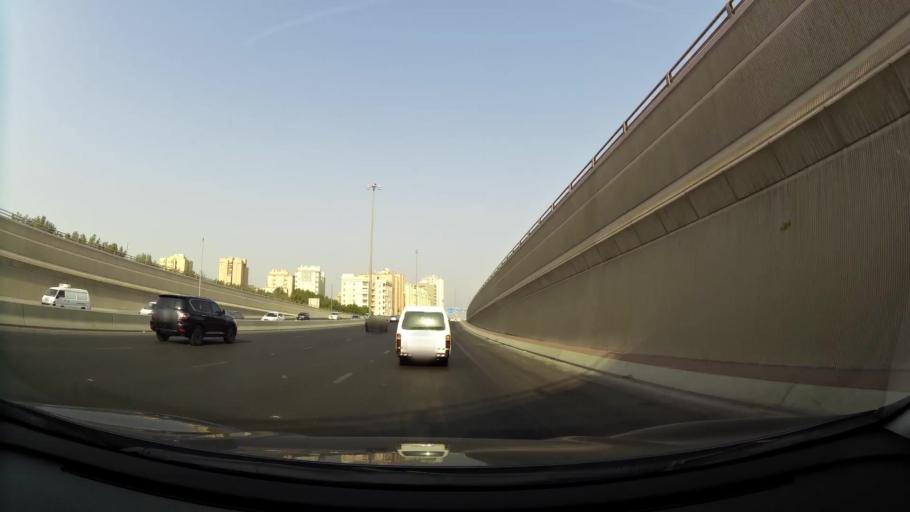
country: KW
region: Muhafazat Hawalli
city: Ar Rumaythiyah
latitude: 29.3235
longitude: 48.0665
